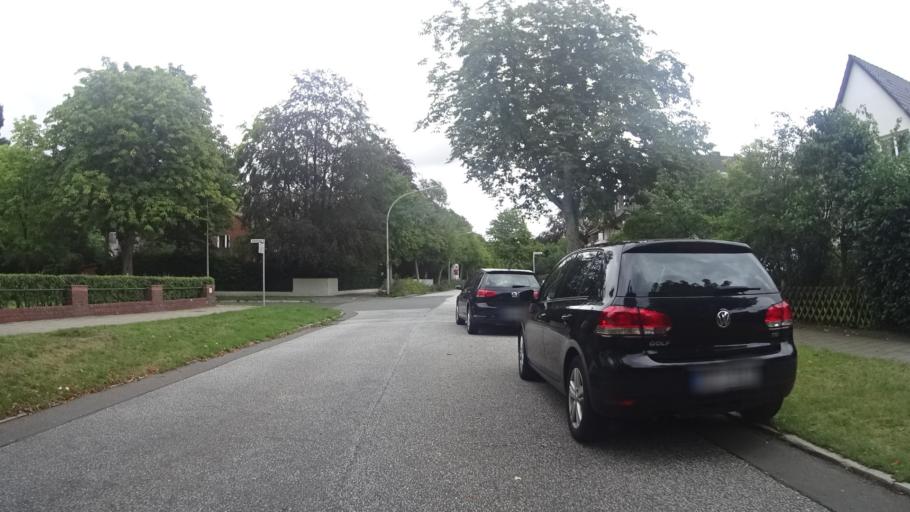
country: DE
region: Bremen
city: Bremerhaven
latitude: 53.5353
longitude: 8.6071
